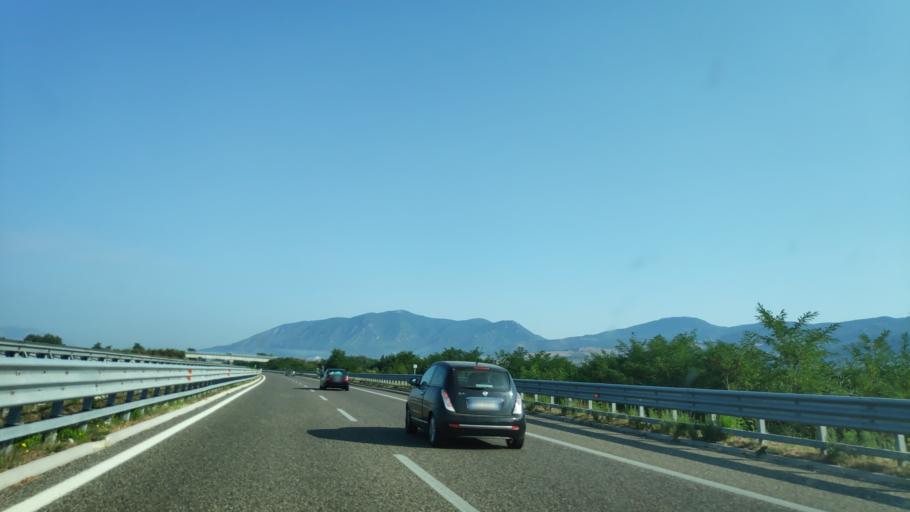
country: IT
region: Campania
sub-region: Provincia di Salerno
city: Padula
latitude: 40.3221
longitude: 15.6378
